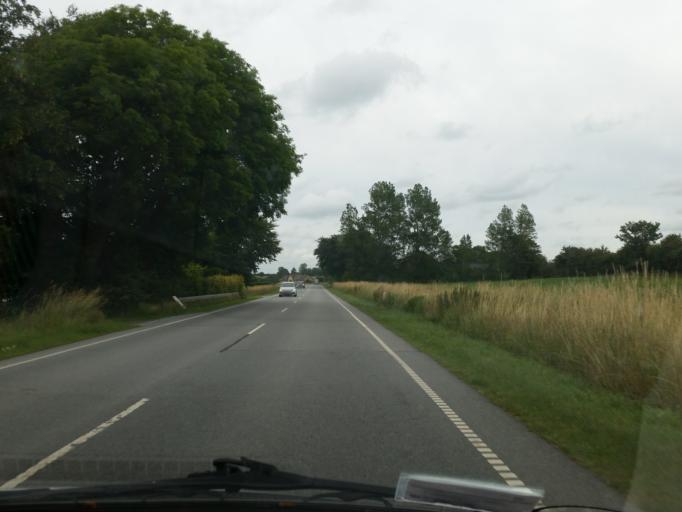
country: DK
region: South Denmark
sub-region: Vejen Kommune
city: Holsted
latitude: 55.4014
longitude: 8.9259
